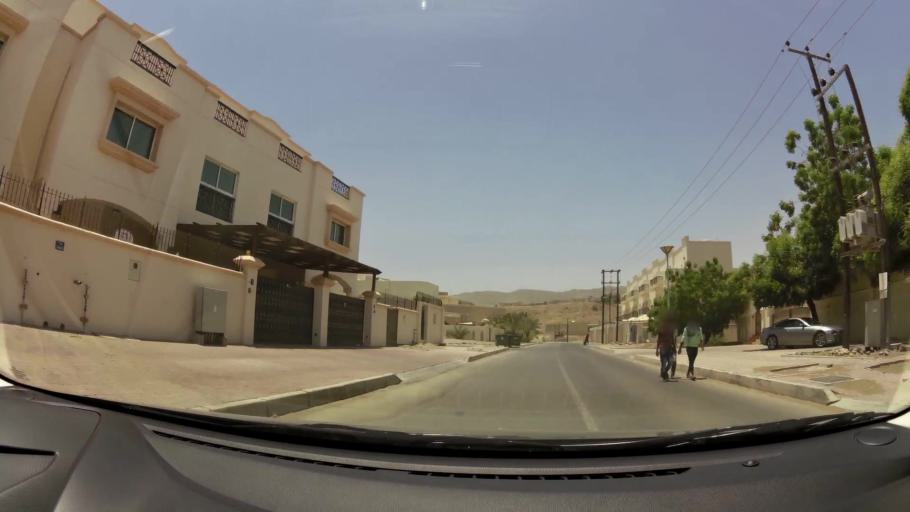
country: OM
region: Muhafazat Masqat
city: Bawshar
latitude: 23.6051
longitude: 58.4632
